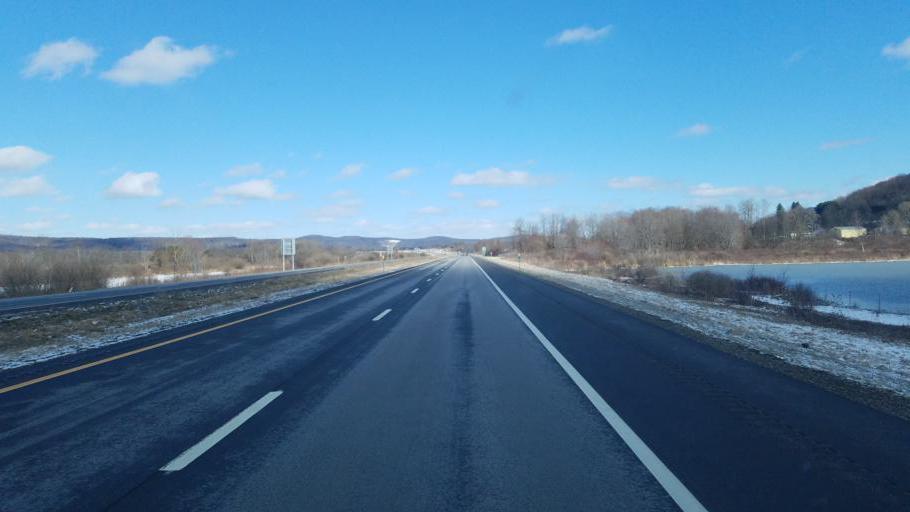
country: US
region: New York
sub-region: Cattaraugus County
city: Allegany
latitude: 42.0908
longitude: -78.5547
